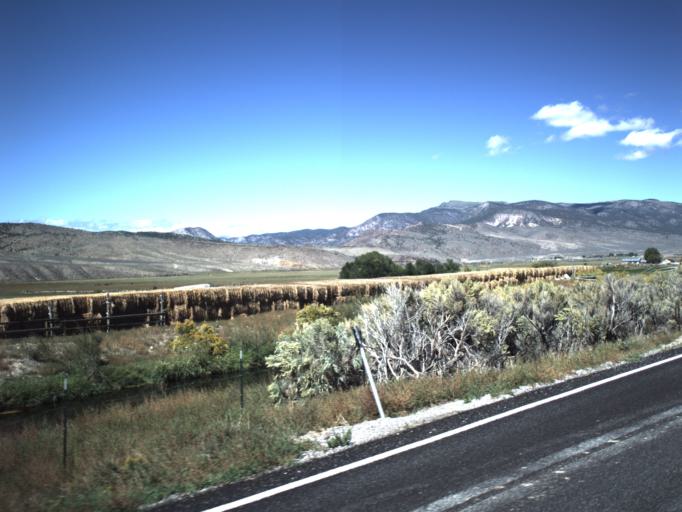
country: US
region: Utah
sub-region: Piute County
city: Junction
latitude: 38.1276
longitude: -112.0003
